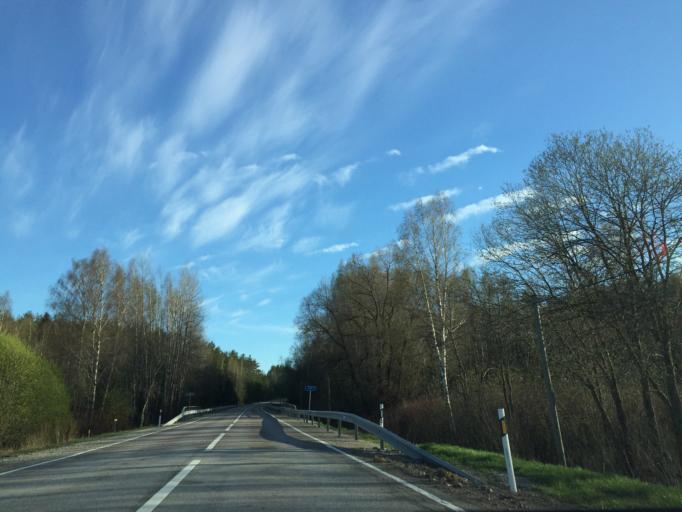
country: LV
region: Valkas Rajons
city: Valka
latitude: 57.7388
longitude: 25.9452
